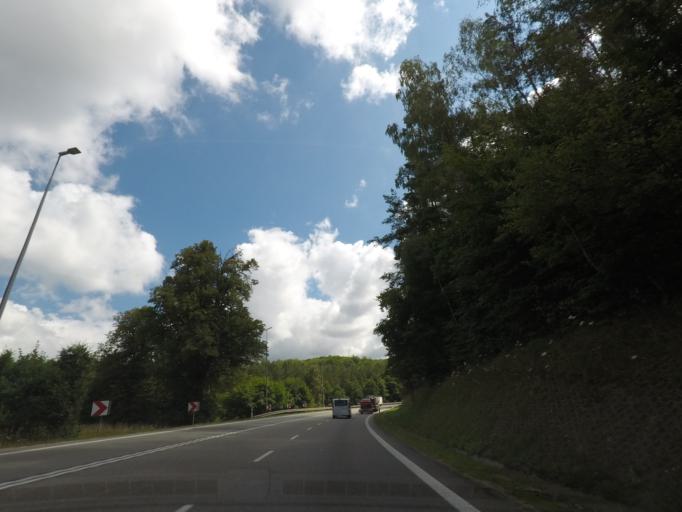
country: PL
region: Pomeranian Voivodeship
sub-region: Powiat wejherowski
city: Luzino
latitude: 54.5806
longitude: 18.0697
